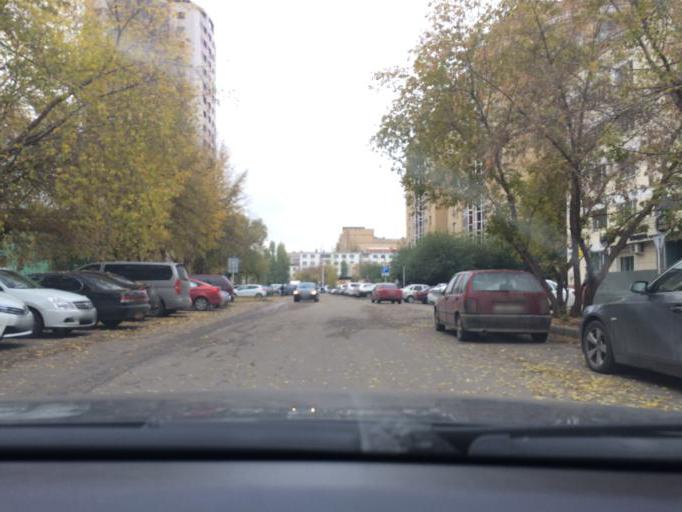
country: KZ
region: Astana Qalasy
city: Astana
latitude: 51.1649
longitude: 71.4380
